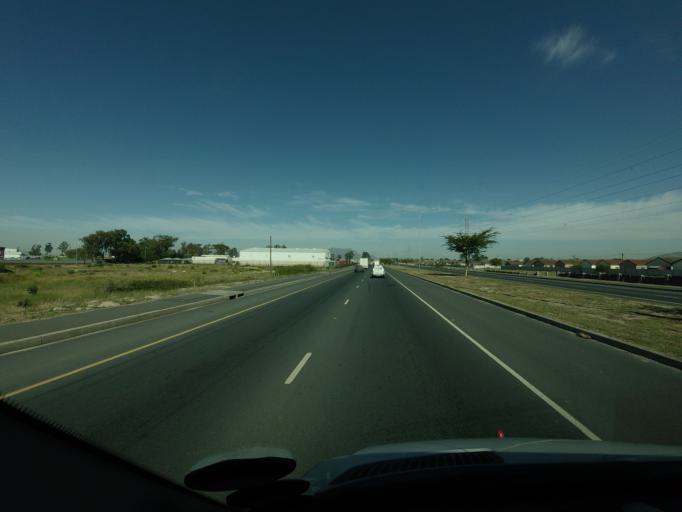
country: ZA
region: Western Cape
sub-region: City of Cape Town
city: Kraaifontein
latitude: -33.9561
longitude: 18.6752
